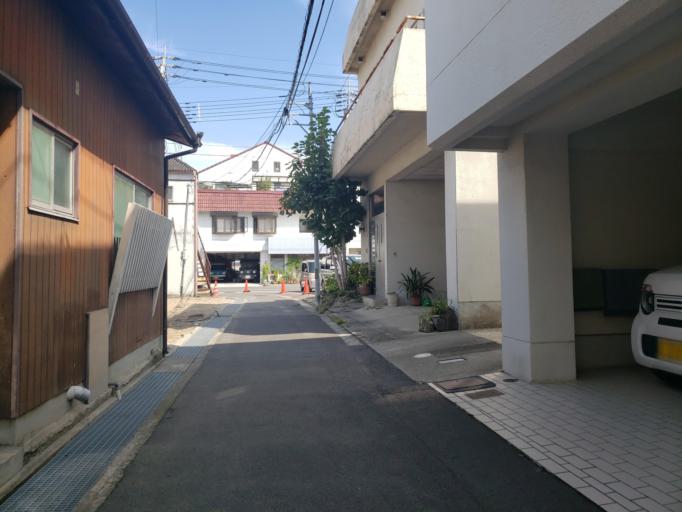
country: JP
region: Kagawa
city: Marugame
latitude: 34.2270
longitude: 133.7810
